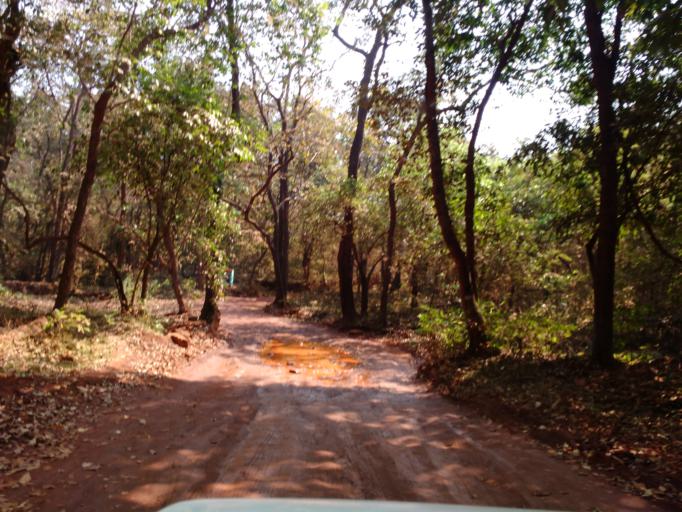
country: IN
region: Goa
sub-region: South Goa
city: Sanguem
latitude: 15.3406
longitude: 74.2543
